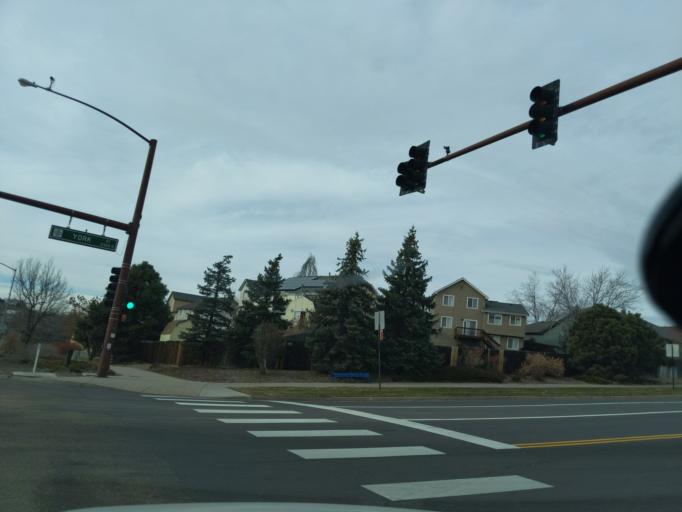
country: US
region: Colorado
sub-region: Adams County
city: Thornton
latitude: 39.8707
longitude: -104.9588
